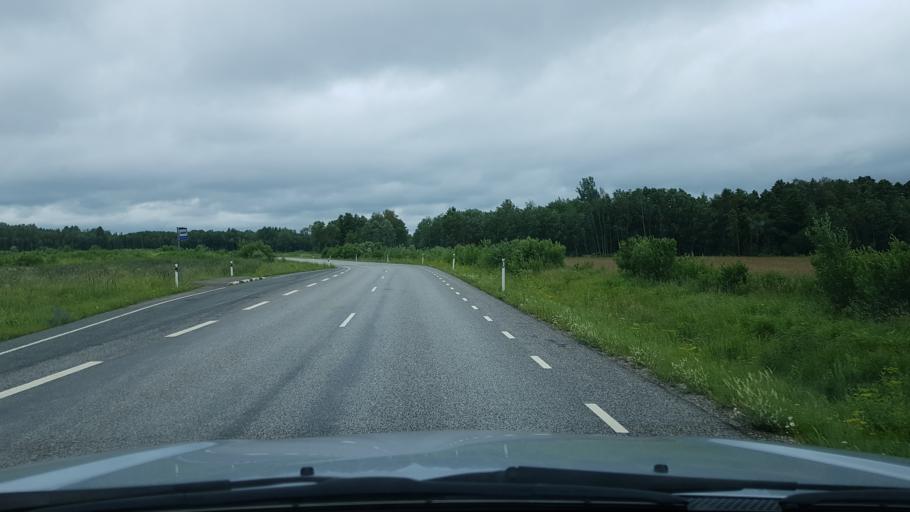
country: EE
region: Ida-Virumaa
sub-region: Narva-Joesuu linn
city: Narva-Joesuu
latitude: 59.3712
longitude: 27.9299
